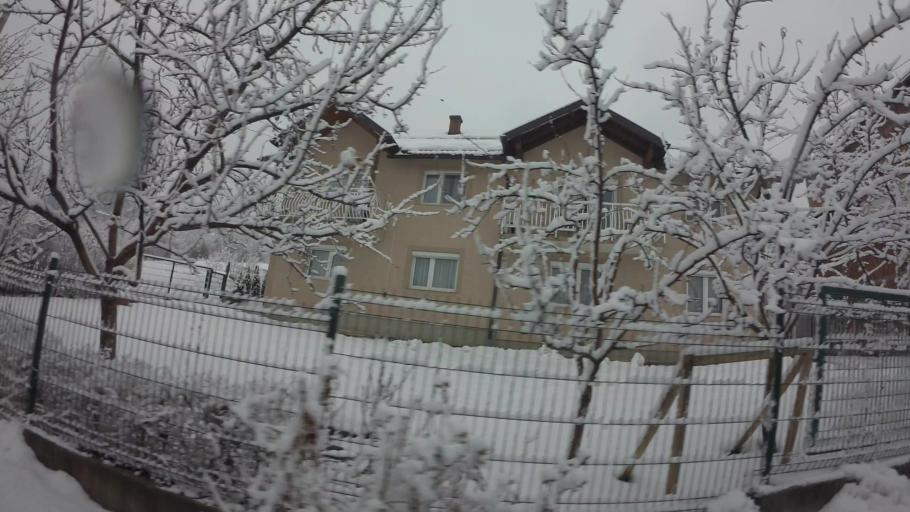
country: BA
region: Federation of Bosnia and Herzegovina
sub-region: Kanton Sarajevo
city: Sarajevo
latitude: 43.8624
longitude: 18.3231
